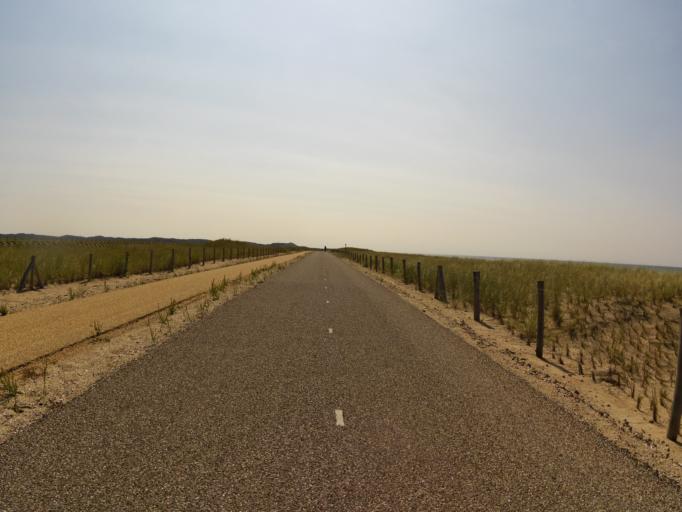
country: NL
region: North Holland
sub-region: Gemeente Bergen
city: Egmond aan Zee
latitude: 52.7448
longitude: 4.6451
